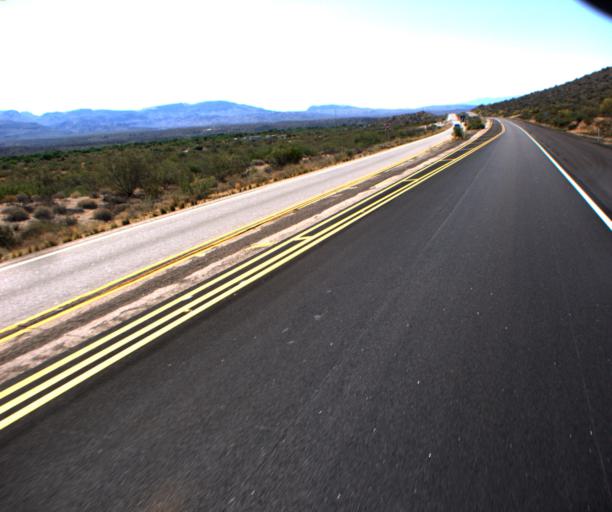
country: US
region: Arizona
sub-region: Yavapai County
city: Bagdad
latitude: 34.6899
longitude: -113.6036
